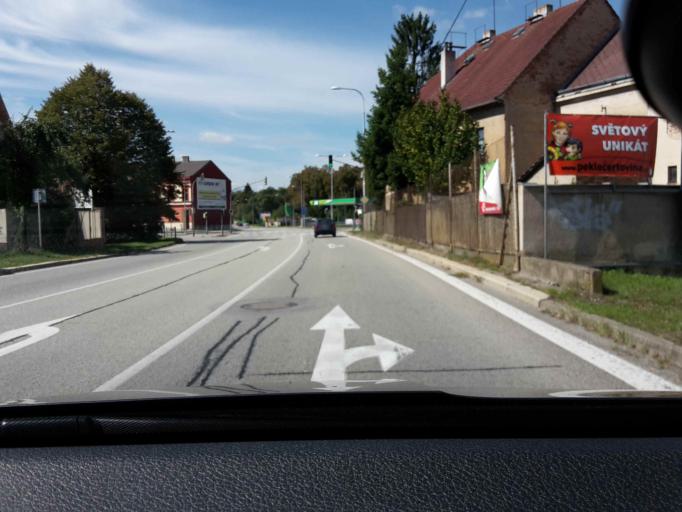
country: CZ
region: Jihocesky
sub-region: Okres Jindrichuv Hradec
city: Jindrichuv Hradec
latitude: 49.1540
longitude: 15.0041
